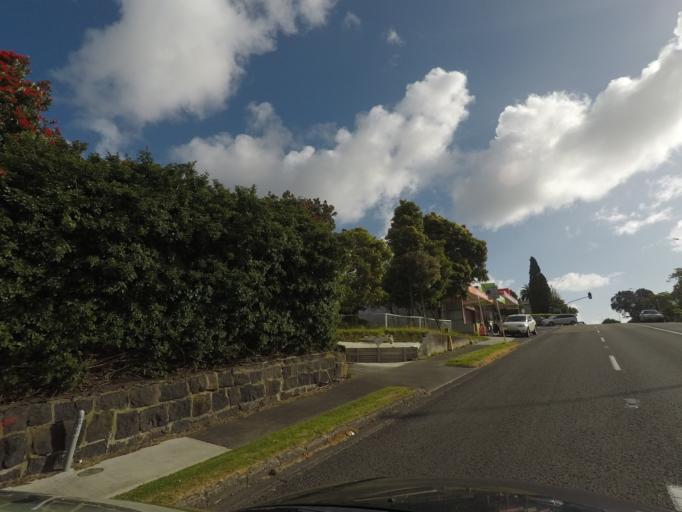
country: NZ
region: Auckland
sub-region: Auckland
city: Auckland
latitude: -36.9211
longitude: 174.7560
